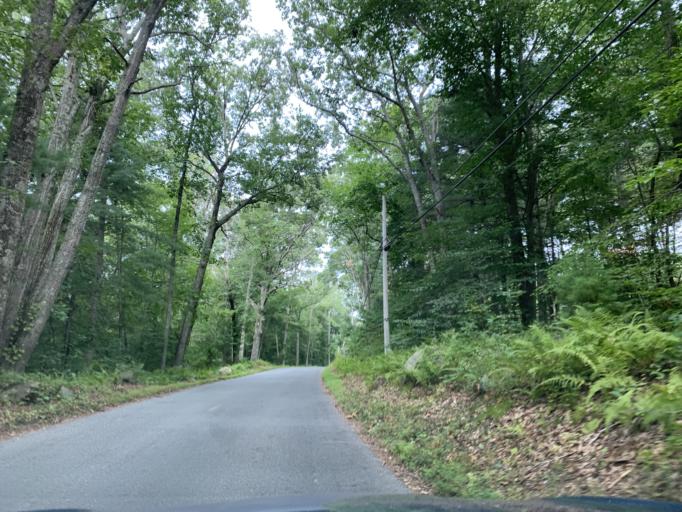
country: US
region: Rhode Island
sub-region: Kent County
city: West Greenwich
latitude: 41.5692
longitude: -71.6209
